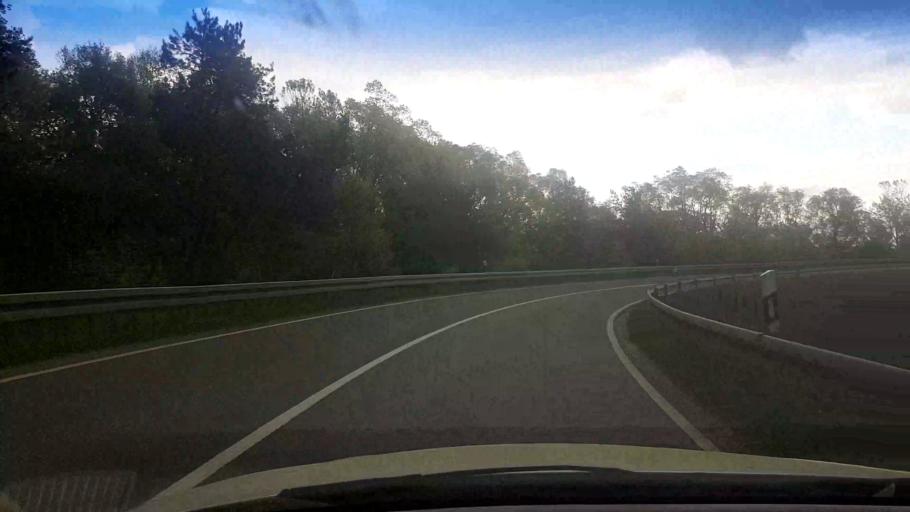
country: DE
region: Bavaria
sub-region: Upper Franconia
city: Pettstadt
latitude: 49.8303
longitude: 10.9517
